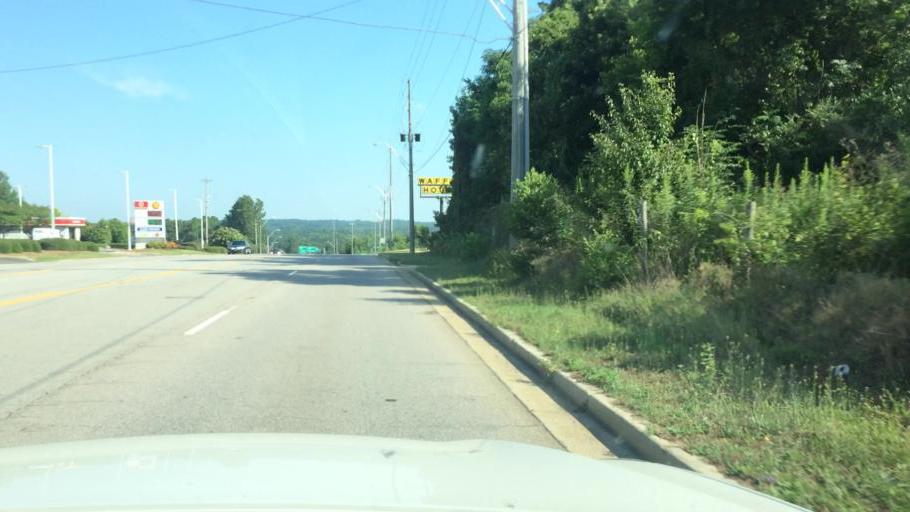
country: US
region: South Carolina
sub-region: Aiken County
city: North Augusta
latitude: 33.5357
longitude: -81.9879
